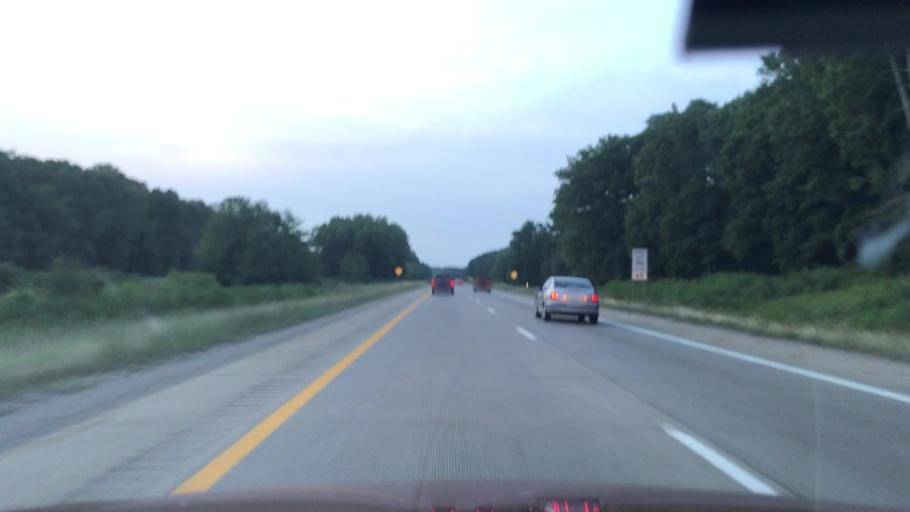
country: US
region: Michigan
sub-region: Kent County
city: Comstock Park
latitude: 43.0543
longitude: -85.6627
